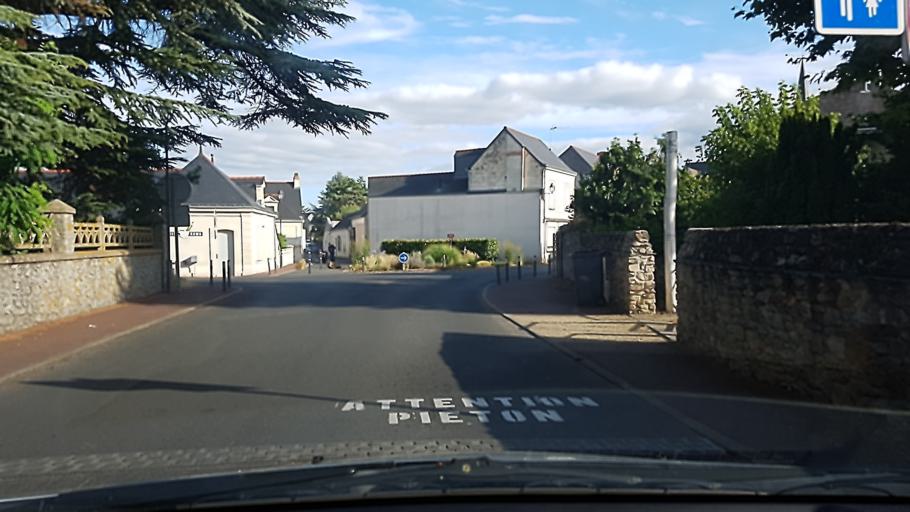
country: FR
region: Pays de la Loire
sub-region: Departement de Maine-et-Loire
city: Maze
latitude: 47.4576
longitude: -0.2720
